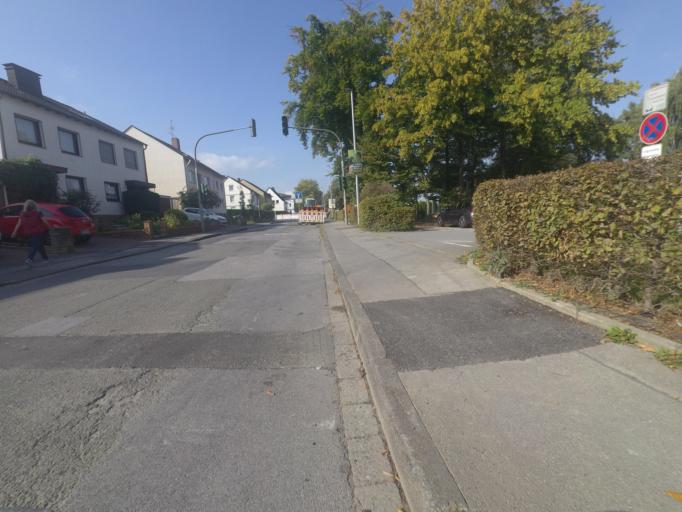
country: DE
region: North Rhine-Westphalia
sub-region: Regierungsbezirk Arnsberg
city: Frondenberg
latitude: 51.4597
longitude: 7.7252
